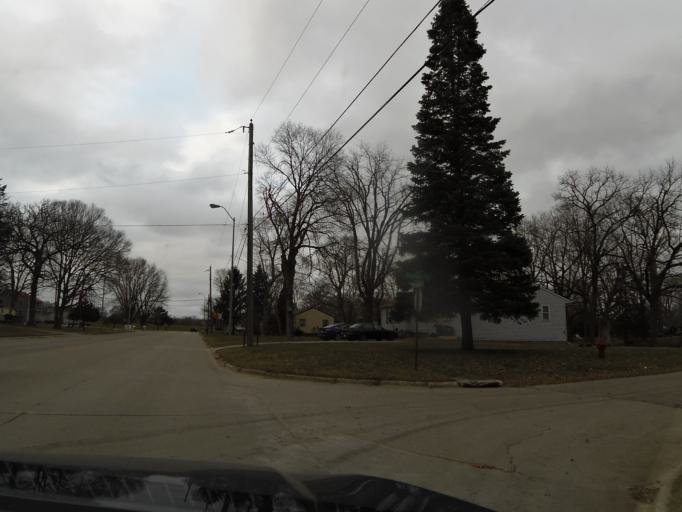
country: US
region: Iowa
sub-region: Black Hawk County
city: Evansdale
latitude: 42.4675
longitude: -92.2975
